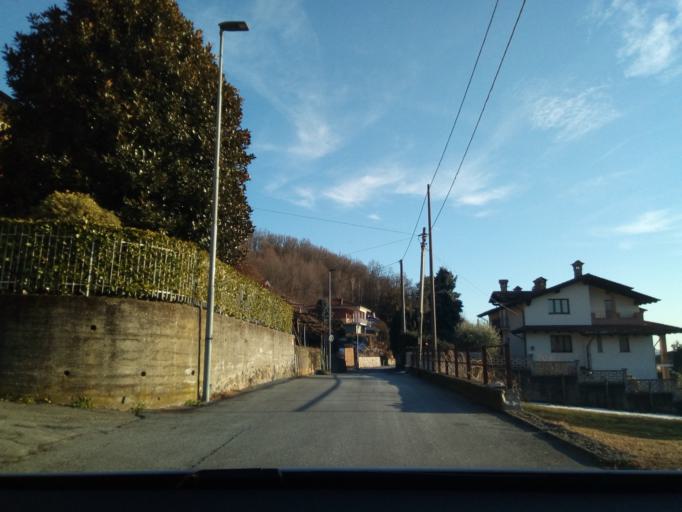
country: IT
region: Piedmont
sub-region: Provincia di Torino
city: Burolo
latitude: 45.4803
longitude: 7.9365
